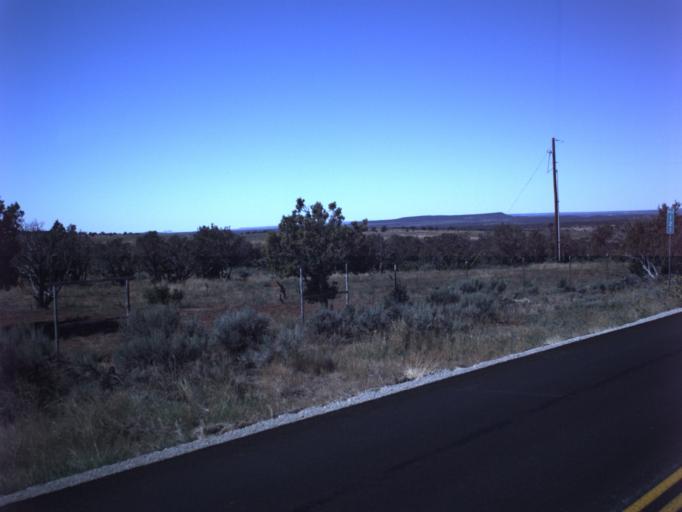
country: US
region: Utah
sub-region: San Juan County
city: Blanding
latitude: 37.5736
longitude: -109.4932
